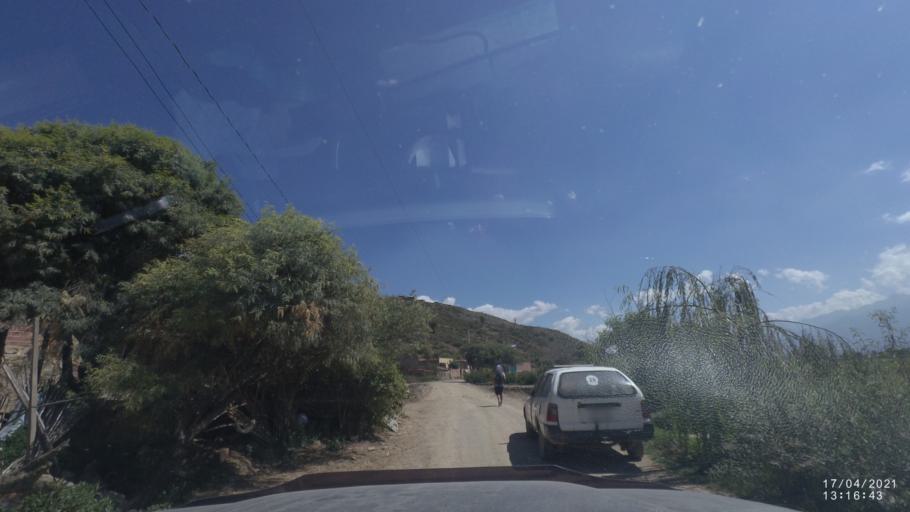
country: BO
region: Cochabamba
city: Cochabamba
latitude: -17.4168
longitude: -66.2384
